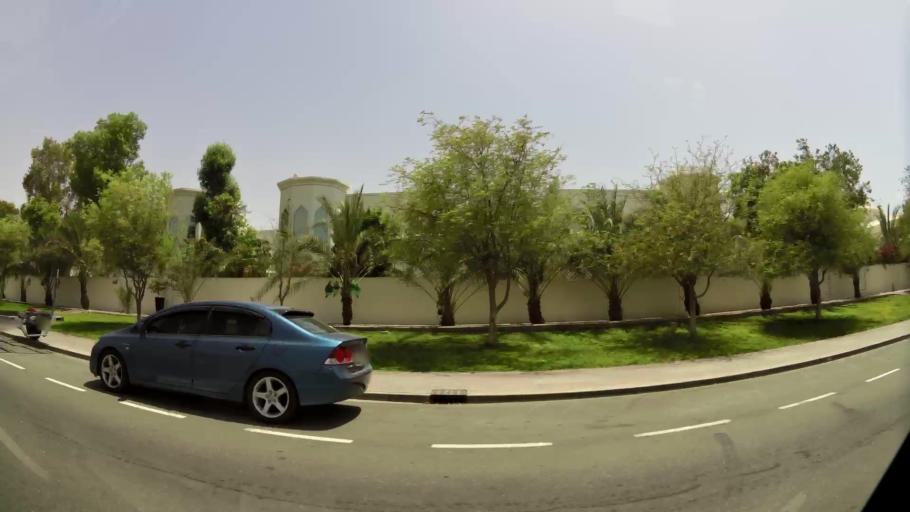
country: AE
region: Dubai
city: Dubai
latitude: 25.1423
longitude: 55.1957
